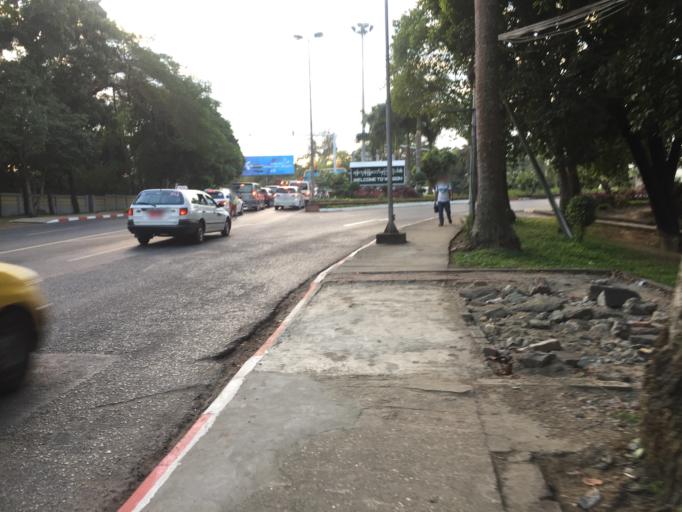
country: MM
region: Yangon
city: Yangon
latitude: 16.8900
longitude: 96.1321
